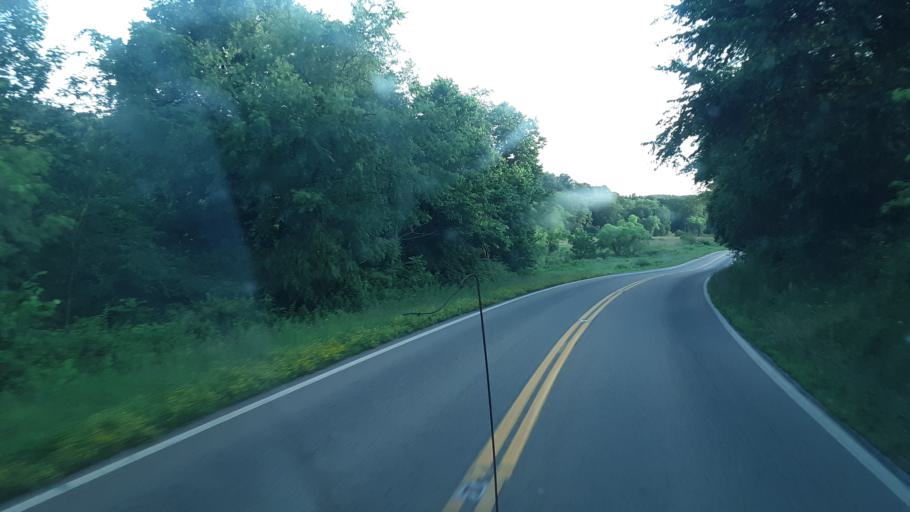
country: US
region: Ohio
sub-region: Harrison County
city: Cadiz
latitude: 40.4015
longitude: -81.0677
